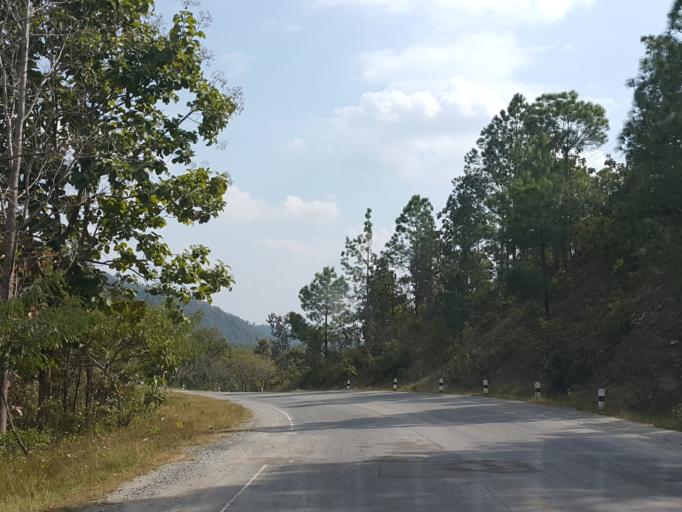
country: TH
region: Chiang Mai
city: Om Koi
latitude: 17.8185
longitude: 98.3668
